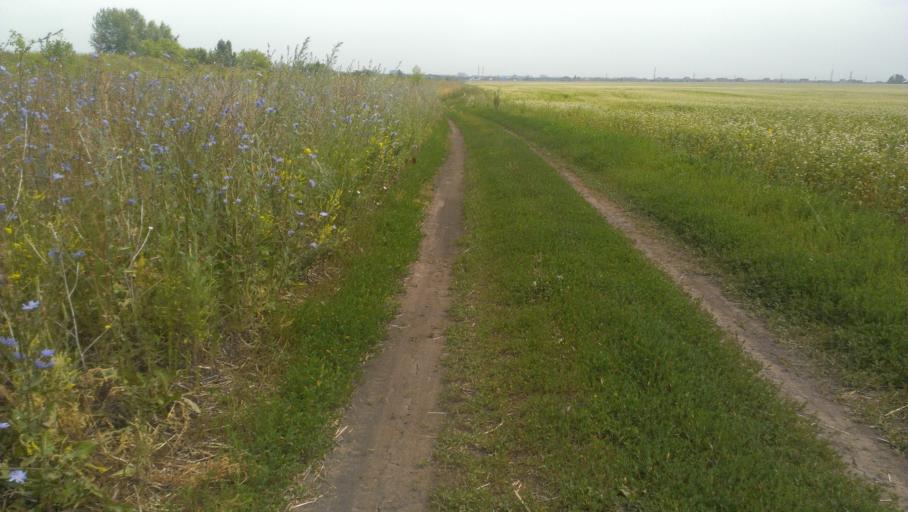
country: RU
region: Altai Krai
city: Gon'ba
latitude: 53.3799
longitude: 83.6326
